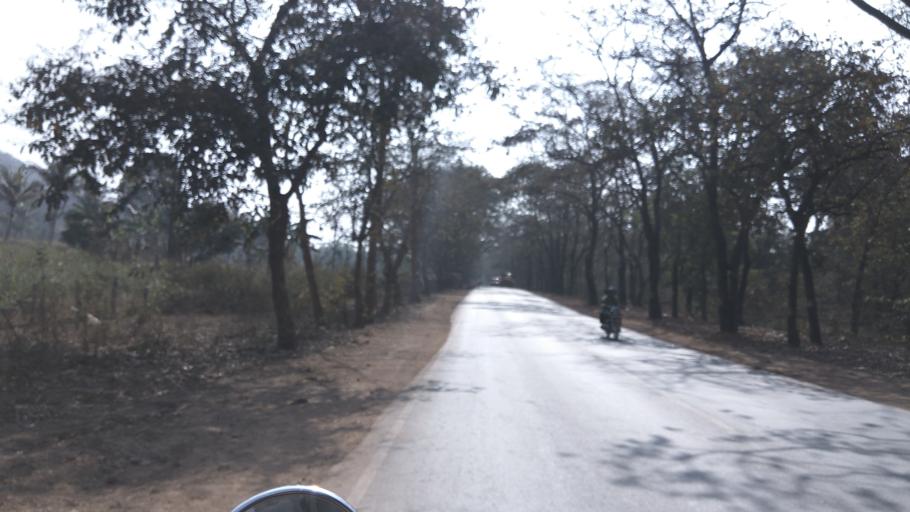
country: IN
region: Goa
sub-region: North Goa
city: Palle
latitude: 15.4014
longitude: 74.0990
